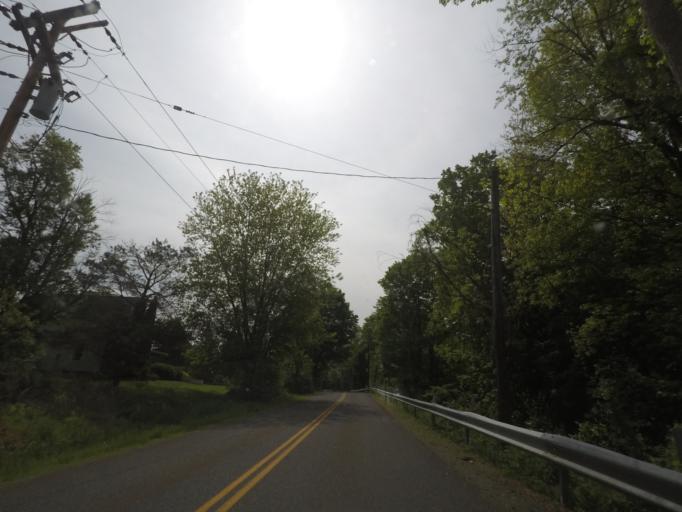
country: US
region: New York
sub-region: Saratoga County
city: Mechanicville
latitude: 42.9248
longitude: -73.7346
